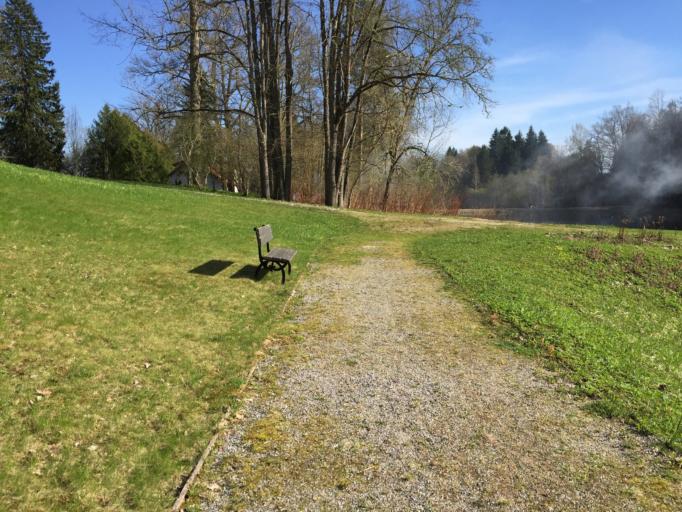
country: EE
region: Vorumaa
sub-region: Antsla vald
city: Vana-Antsla
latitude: 57.9014
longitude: 26.2796
